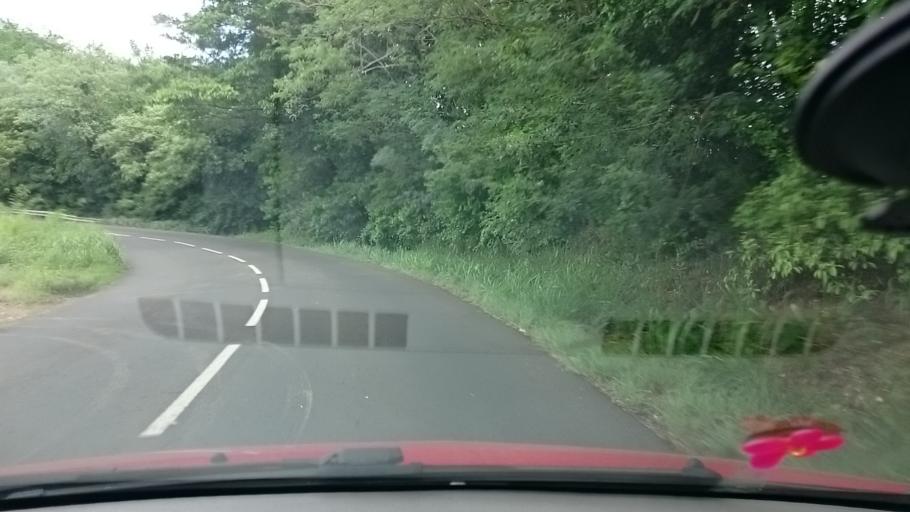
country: MQ
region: Martinique
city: Petite Riviere Salee
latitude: 14.7571
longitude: -60.9361
